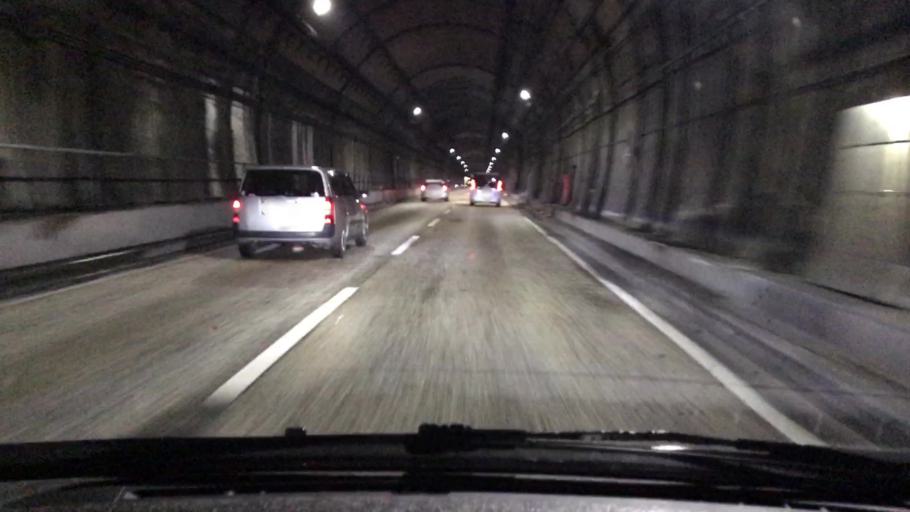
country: JP
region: Hyogo
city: Kobe
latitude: 34.7464
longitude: 135.1687
